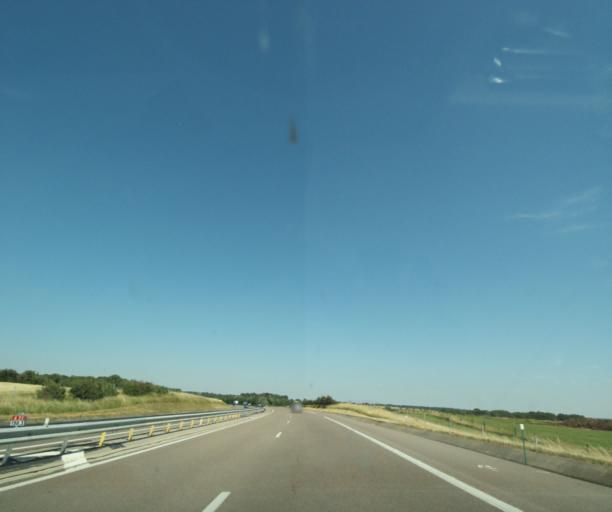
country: FR
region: Lorraine
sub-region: Departement des Vosges
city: Chatenois
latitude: 48.4038
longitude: 5.8785
